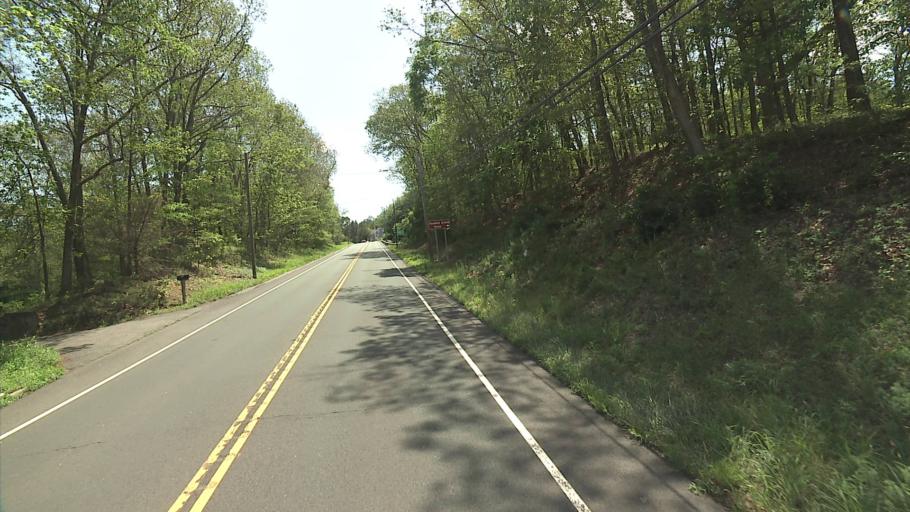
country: US
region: Connecticut
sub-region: Middlesex County
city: Higganum
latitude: 41.4828
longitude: -72.5172
